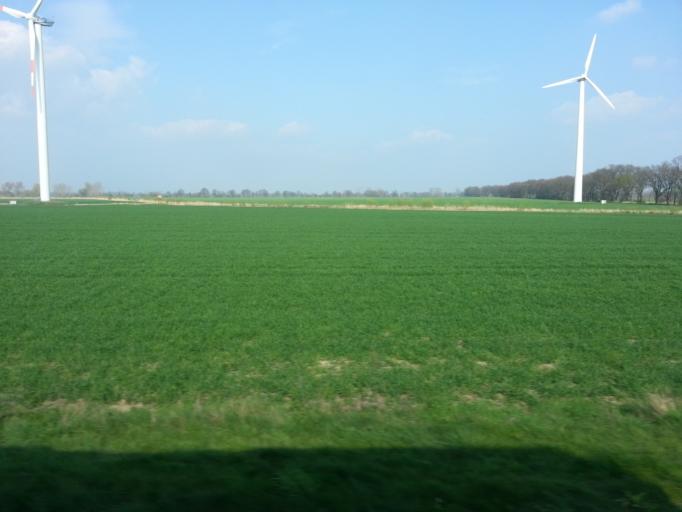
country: DE
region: Brandenburg
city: Dabergotz
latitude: 52.9212
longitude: 12.7166
